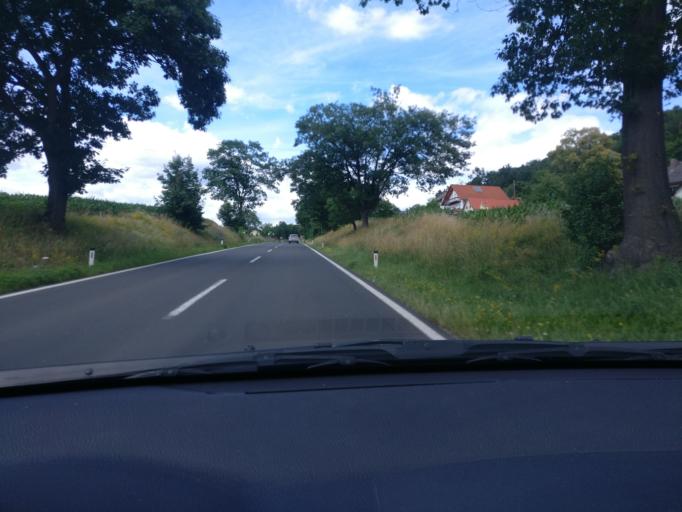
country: AT
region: Styria
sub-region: Politischer Bezirk Hartberg-Fuerstenfeld
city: Kaibing
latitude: 47.2002
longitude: 15.8414
